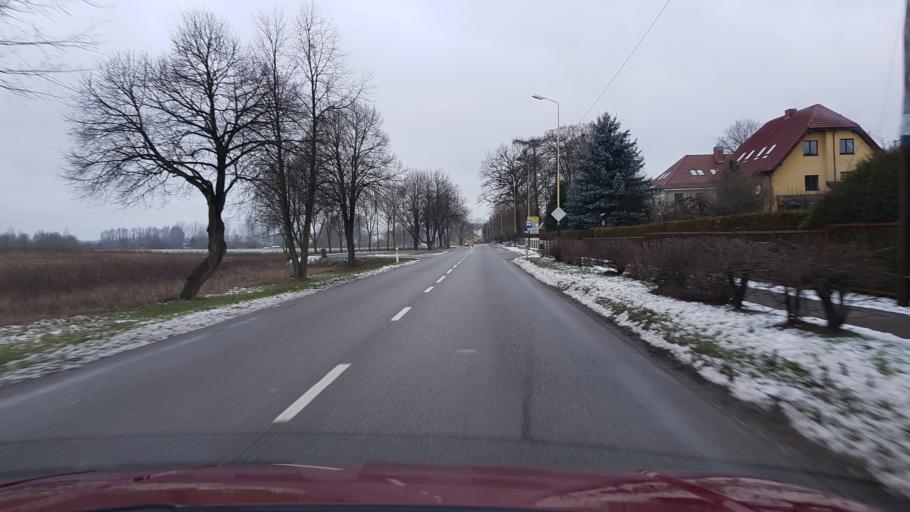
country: PL
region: West Pomeranian Voivodeship
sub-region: Powiat goleniowski
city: Nowogard
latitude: 53.6631
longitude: 15.1561
